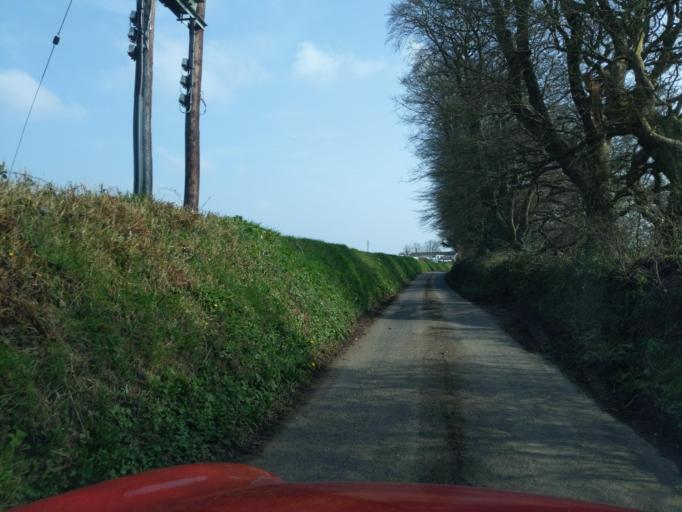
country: GB
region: England
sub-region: Devon
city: Kingsbridge
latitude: 50.3108
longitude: -3.7721
